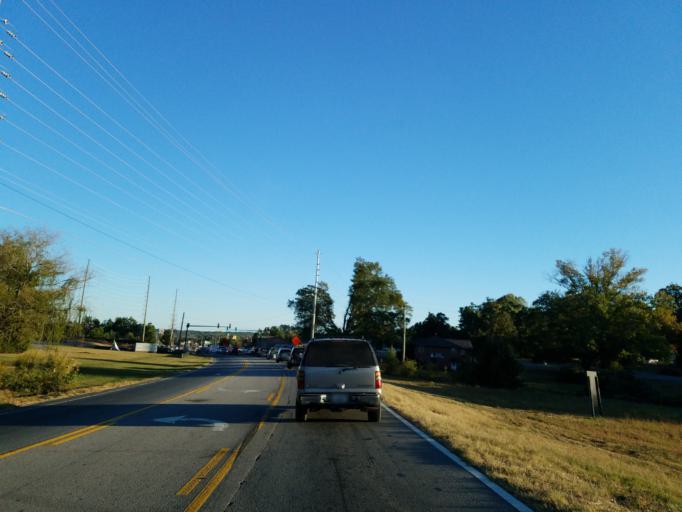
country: US
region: Georgia
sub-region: Dawson County
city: Dawsonville
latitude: 34.3684
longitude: -84.0417
